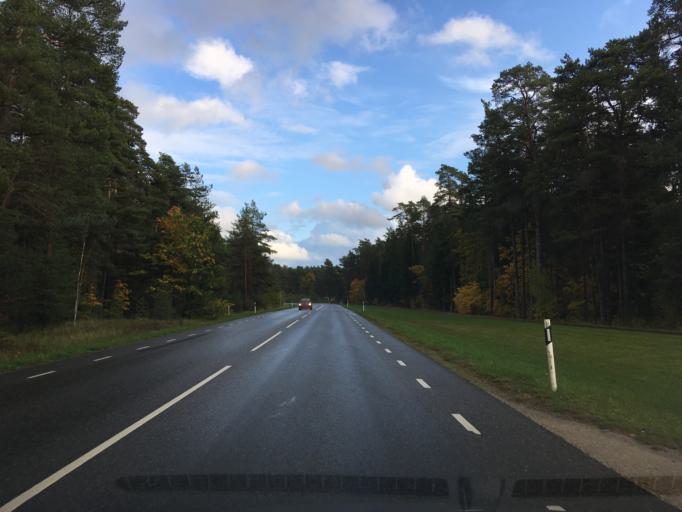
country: EE
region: Harju
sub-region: Paldiski linn
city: Paldiski
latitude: 59.2272
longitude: 24.1473
